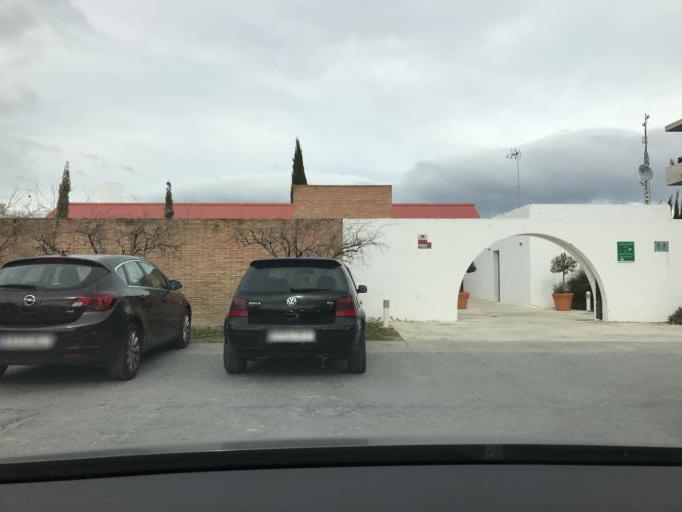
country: ES
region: Andalusia
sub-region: Provincia de Granada
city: Alhendin
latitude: 37.1202
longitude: -3.6616
